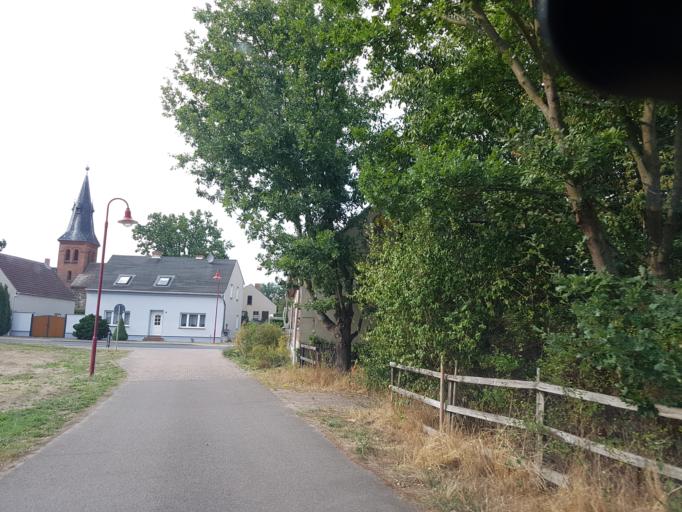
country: DE
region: Saxony-Anhalt
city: Nudersdorf
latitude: 52.0209
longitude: 12.5349
